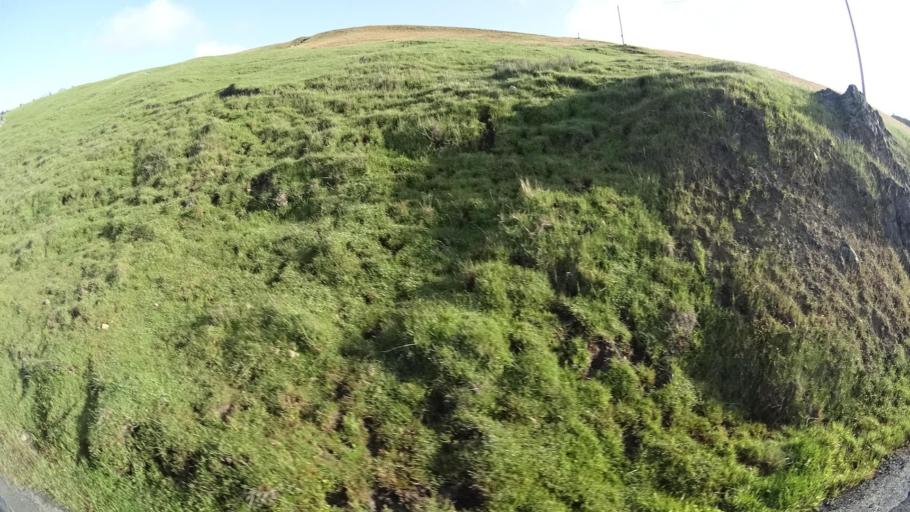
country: US
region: California
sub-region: Humboldt County
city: Blue Lake
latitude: 40.7109
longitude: -123.9374
